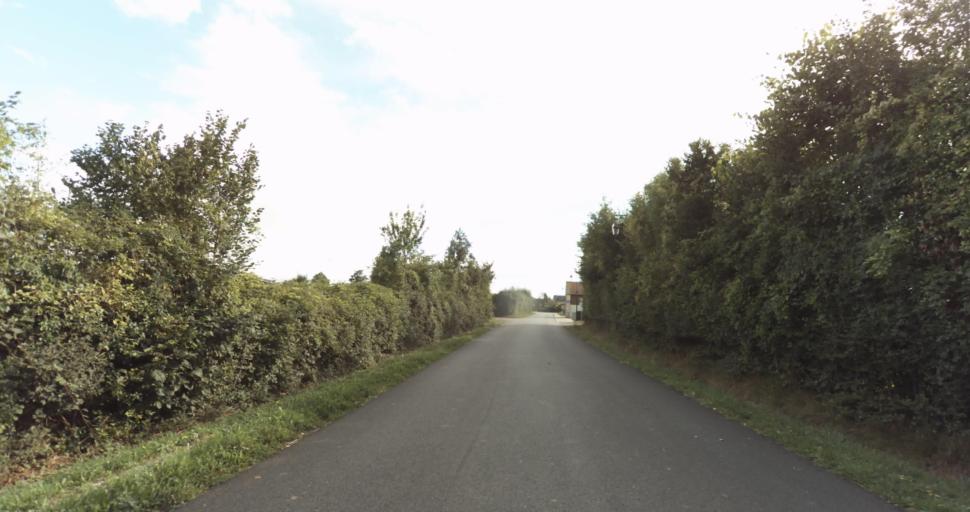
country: FR
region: Lower Normandy
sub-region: Departement de l'Orne
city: Sainte-Gauburge-Sainte-Colombe
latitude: 48.7442
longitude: 0.3874
